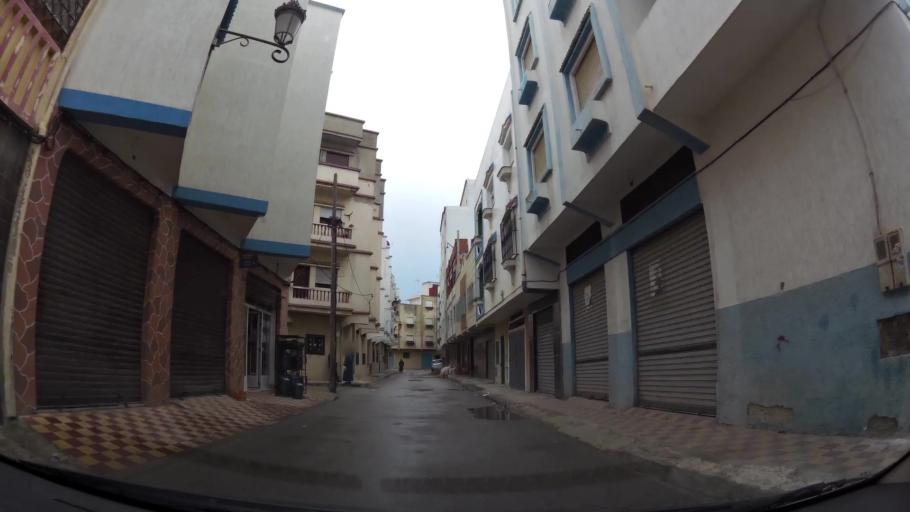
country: MA
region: Tanger-Tetouan
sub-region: Tetouan
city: Martil
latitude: 35.6155
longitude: -5.2838
